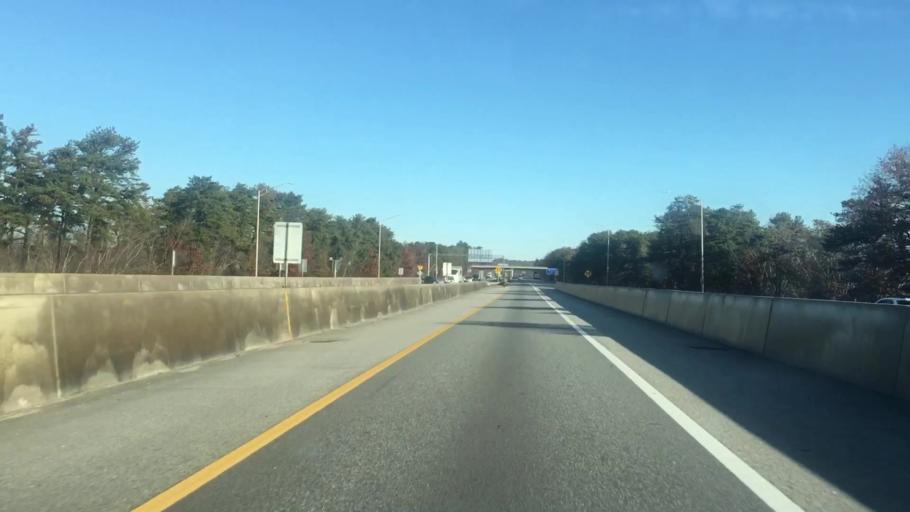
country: US
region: Maine
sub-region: Cumberland County
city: New Gloucester
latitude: 43.9364
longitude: -70.3348
